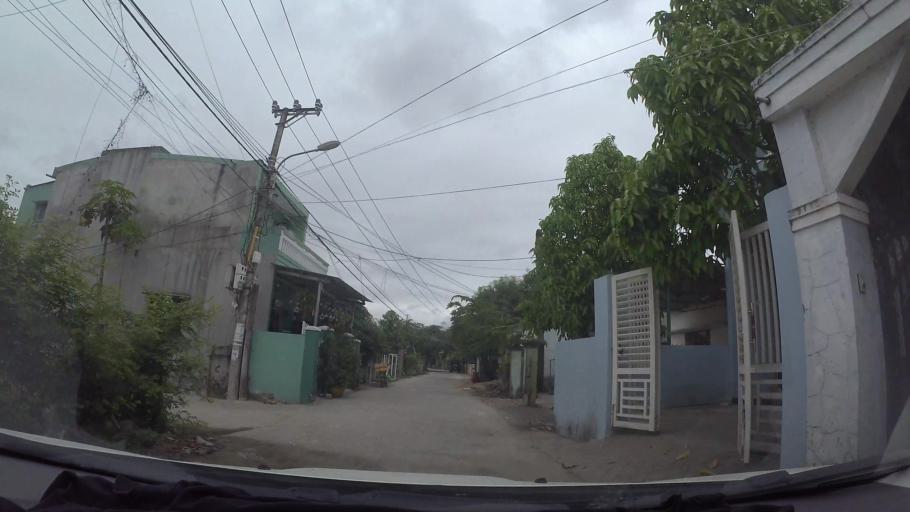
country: VN
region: Da Nang
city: Lien Chieu
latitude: 16.0881
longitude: 108.1023
